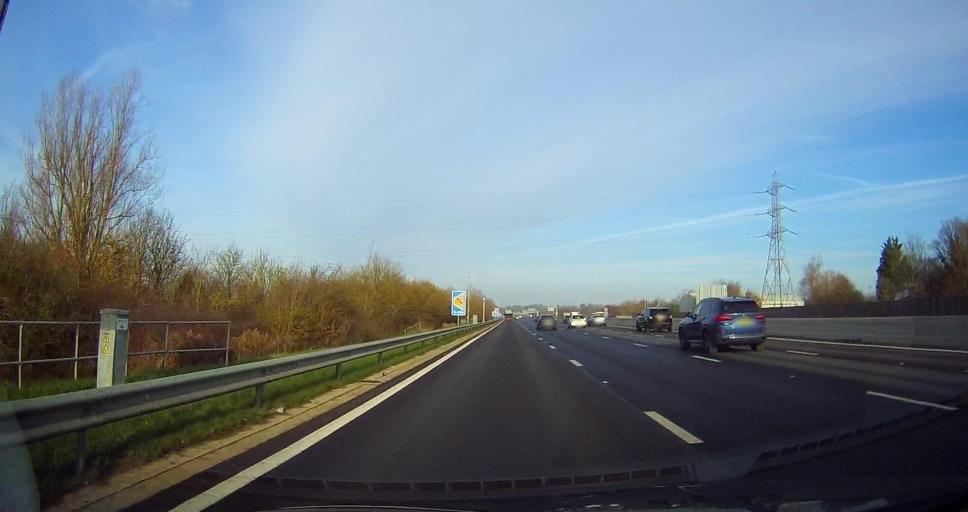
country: GB
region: England
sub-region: Surrey
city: Horley
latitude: 51.1767
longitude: -0.1280
